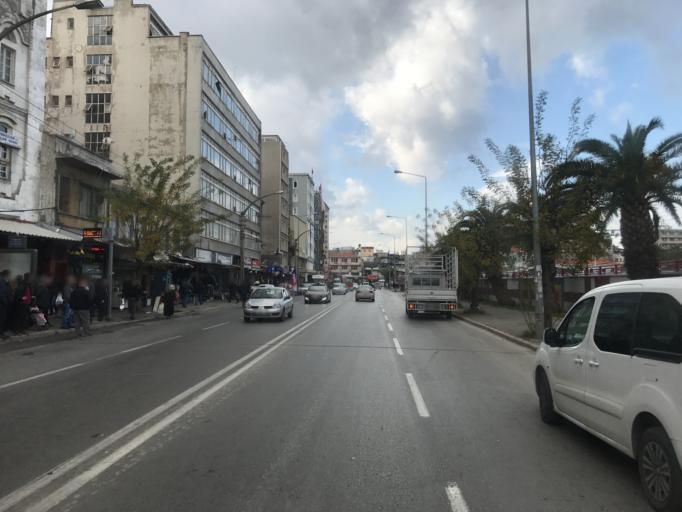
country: TR
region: Izmir
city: Izmir
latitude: 38.4224
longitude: 27.1460
